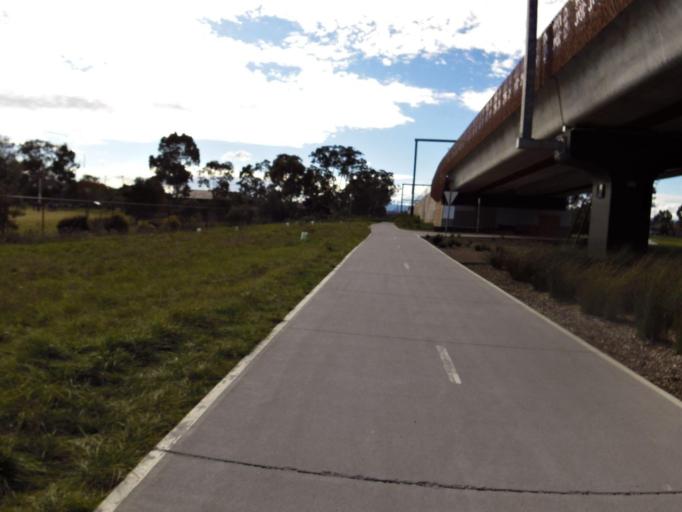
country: AU
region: Victoria
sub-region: Whittlesea
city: Mernda
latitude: -37.6146
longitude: 145.0981
